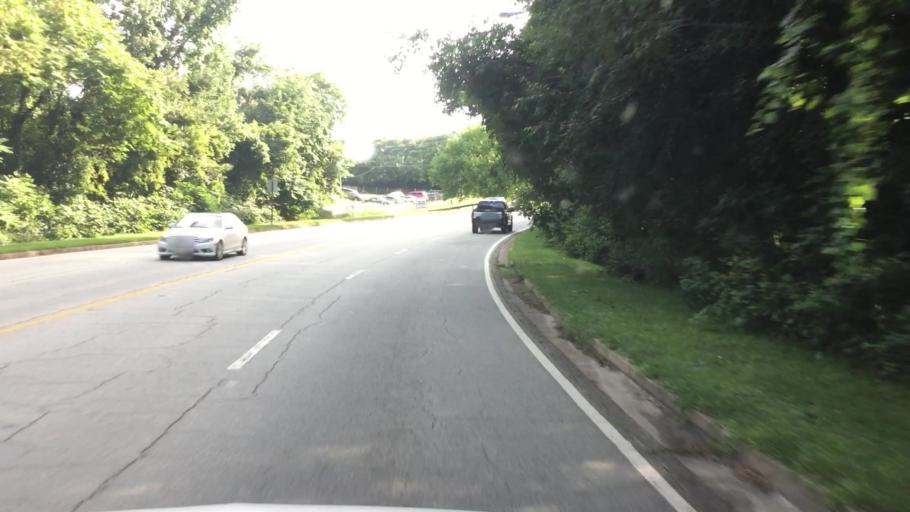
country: US
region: Georgia
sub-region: DeKalb County
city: Lithonia
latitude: 33.7146
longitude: -84.1049
